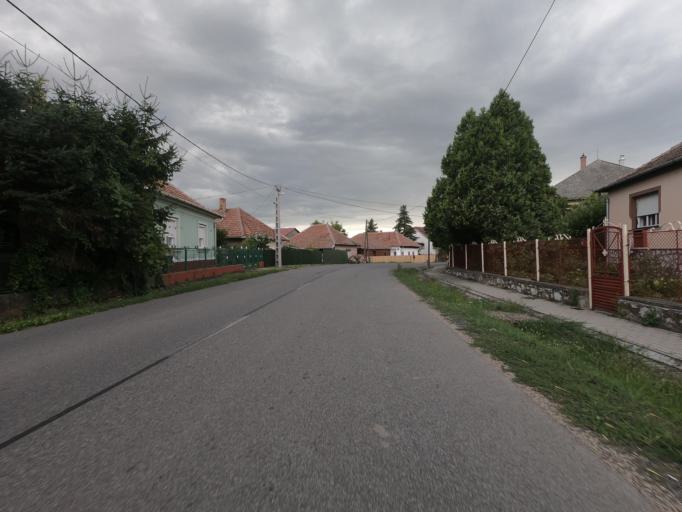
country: HU
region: Heves
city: Poroszlo
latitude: 47.6986
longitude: 20.6576
